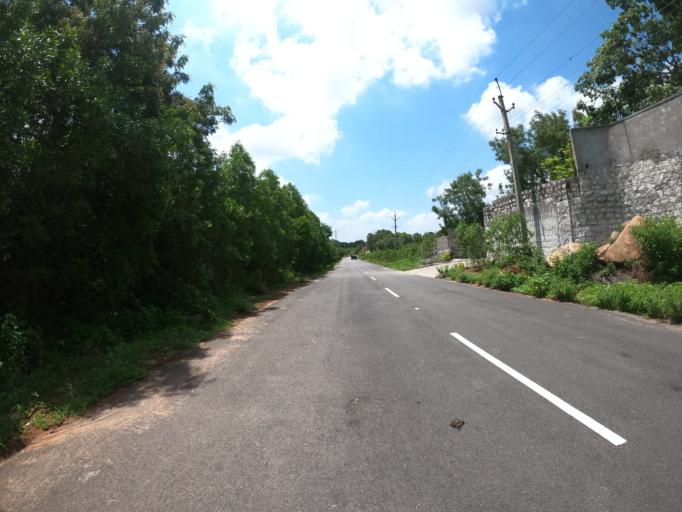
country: IN
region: Telangana
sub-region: Medak
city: Serilingampalle
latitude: 17.3721
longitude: 78.3225
